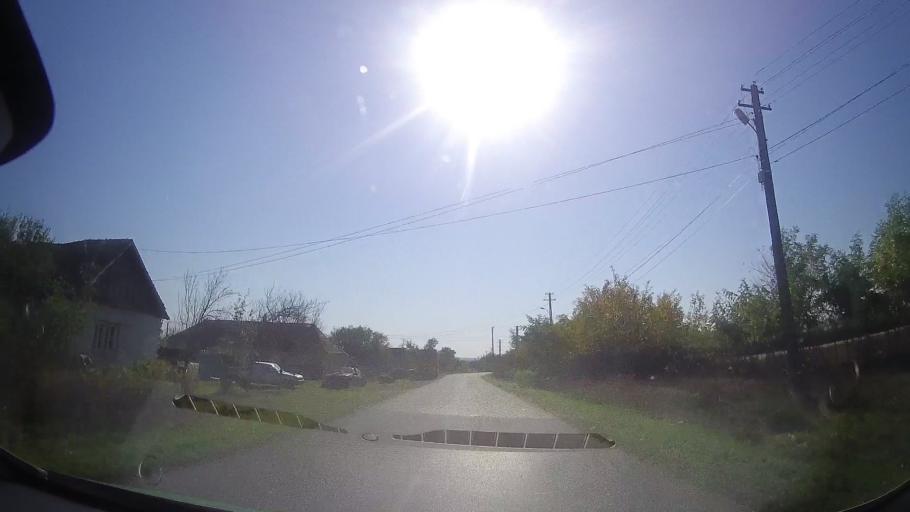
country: RO
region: Timis
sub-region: Comuna Ghizela
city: Ghizela
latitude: 45.8257
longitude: 21.7514
